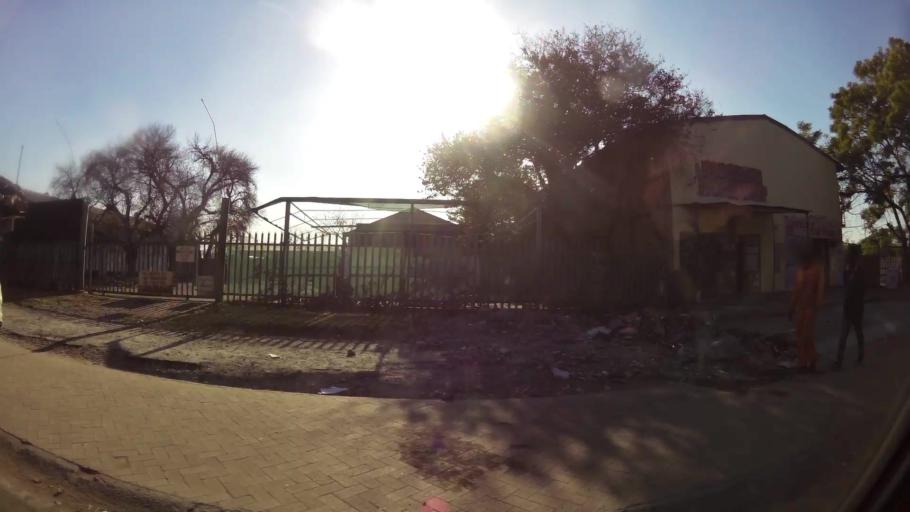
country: ZA
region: North-West
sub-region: Bojanala Platinum District Municipality
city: Rustenburg
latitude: -25.6545
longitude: 27.2371
